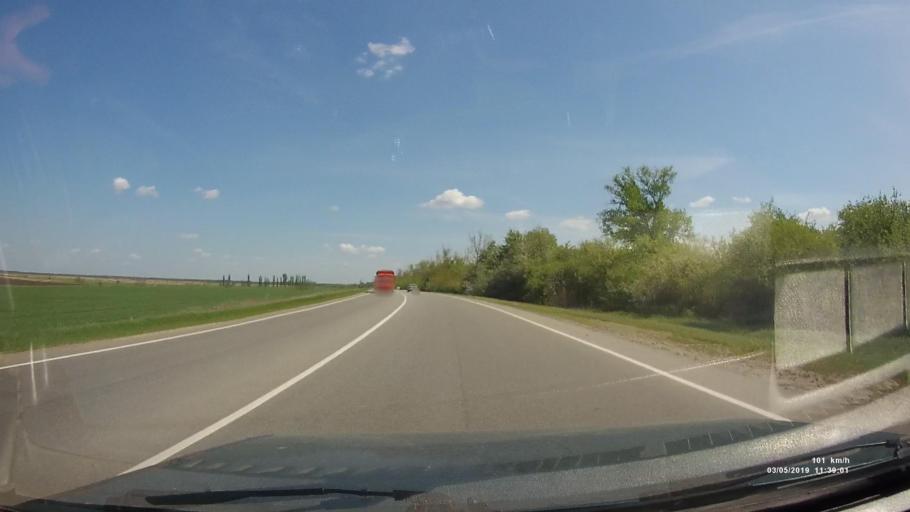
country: RU
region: Rostov
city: Ol'ginskaya
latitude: 47.1311
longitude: 39.9779
